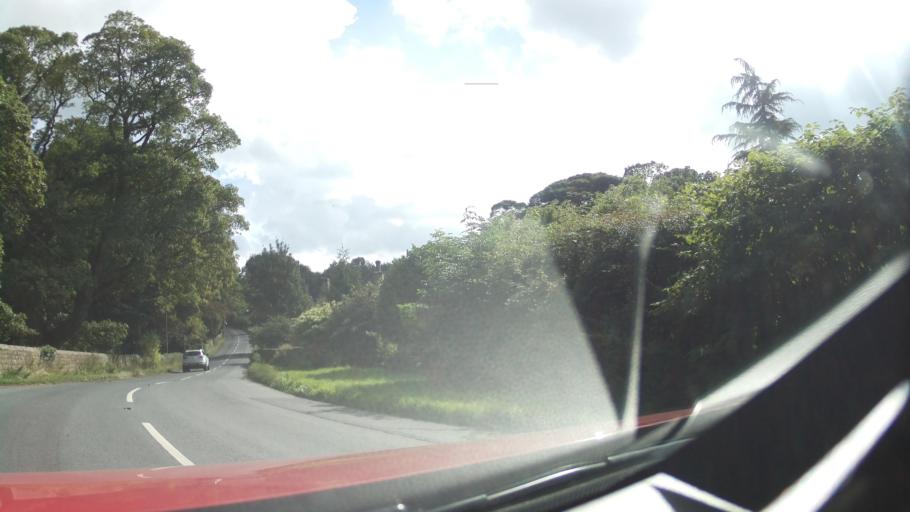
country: GB
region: England
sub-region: North Yorkshire
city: Leyburn
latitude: 54.2672
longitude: -1.7419
